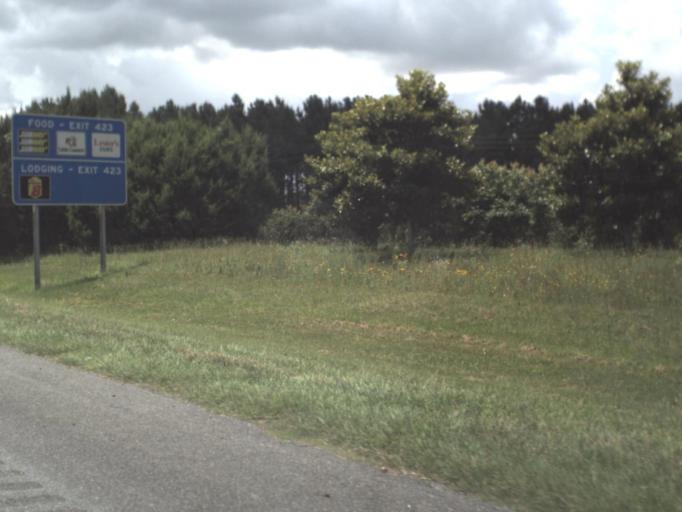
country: US
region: Florida
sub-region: Columbia County
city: Lake City
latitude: 30.1265
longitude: -82.6611
